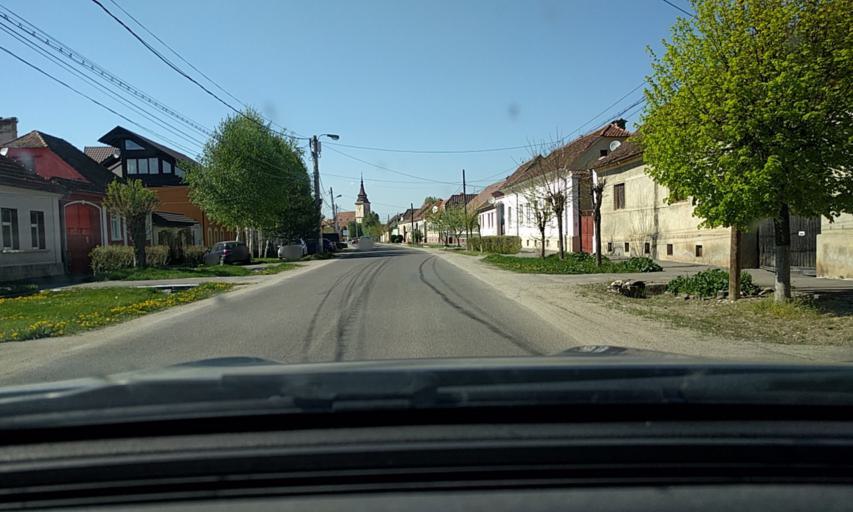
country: RO
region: Brasov
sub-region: Comuna Sanpetru
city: Sanpetru
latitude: 45.7088
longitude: 25.6374
